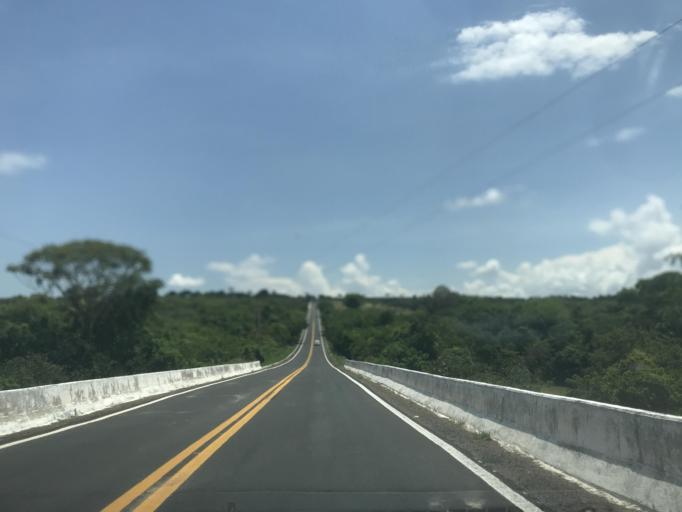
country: BR
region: Goias
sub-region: Bela Vista De Goias
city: Bela Vista de Goias
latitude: -17.1219
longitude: -48.6678
